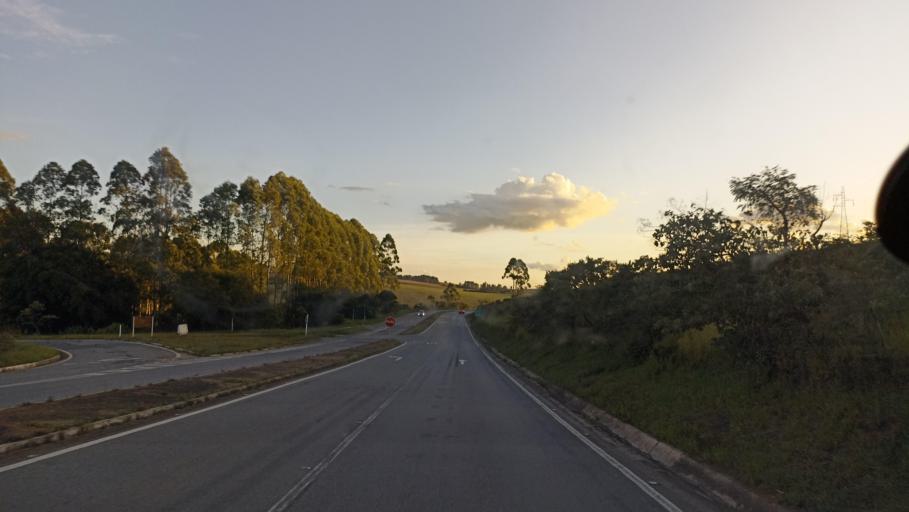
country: BR
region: Minas Gerais
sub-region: Sao Joao Del Rei
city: Sao Joao del Rei
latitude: -21.2280
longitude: -44.3757
